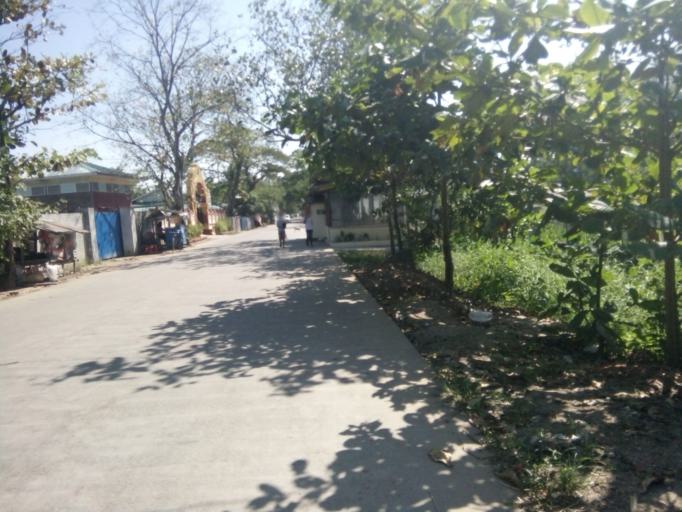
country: MM
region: Yangon
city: Yangon
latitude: 16.9207
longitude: 96.1571
